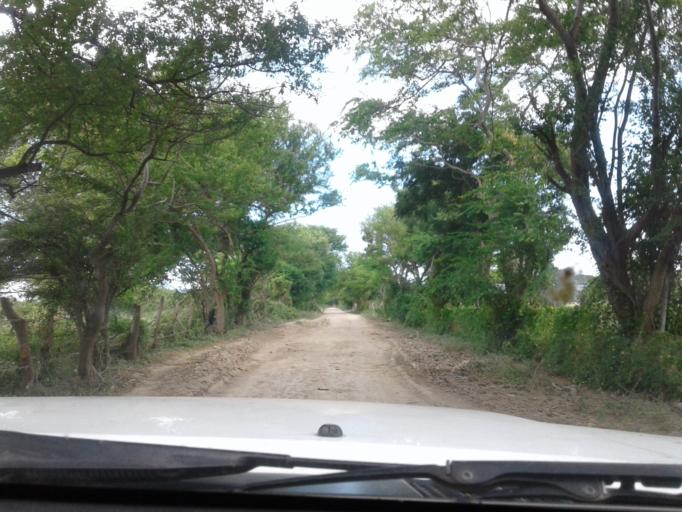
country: NI
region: Rivas
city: Belen
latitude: 11.6619
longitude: -85.8705
